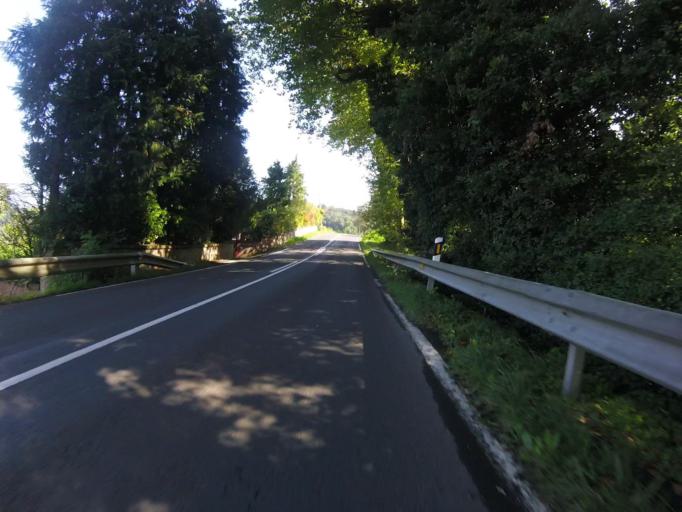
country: ES
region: Basque Country
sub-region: Provincia de Guipuzcoa
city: Lezo
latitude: 43.3071
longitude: -1.8467
